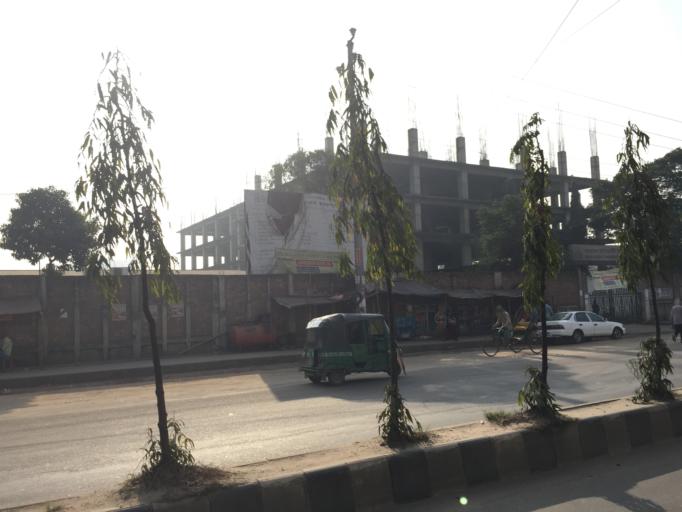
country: BD
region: Dhaka
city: Azimpur
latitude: 23.7835
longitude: 90.3530
